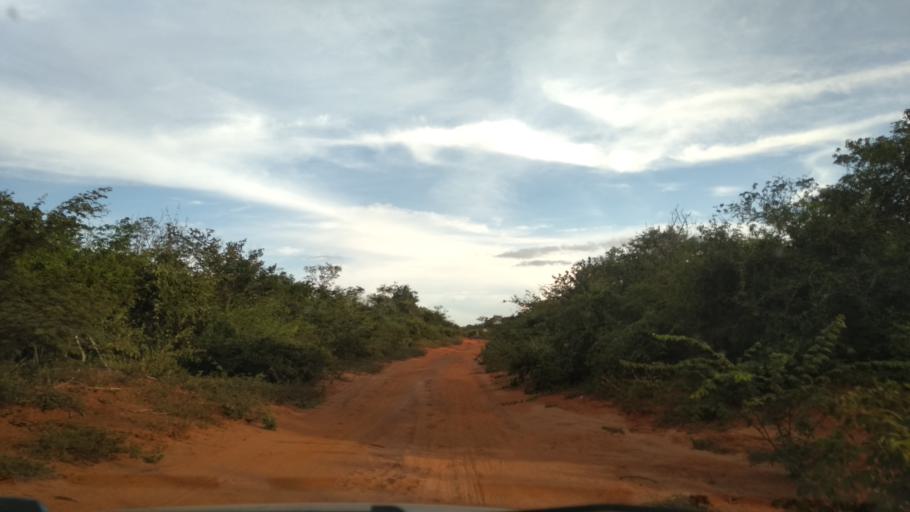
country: BR
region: Bahia
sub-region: Caetite
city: Caetite
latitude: -13.9817
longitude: -42.5111
